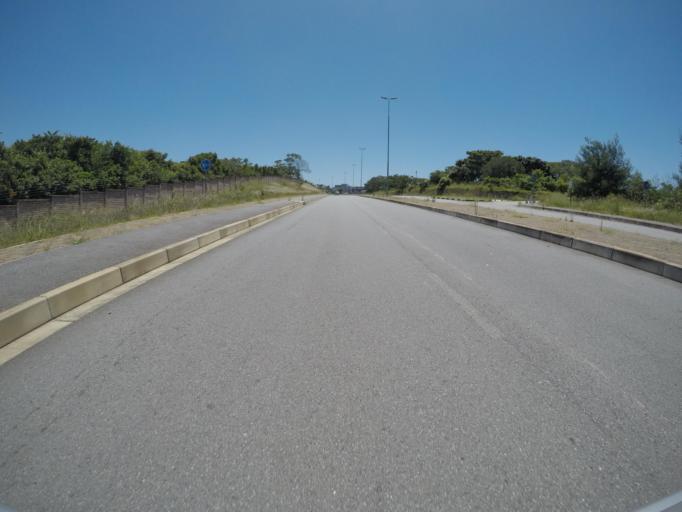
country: ZA
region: Eastern Cape
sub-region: Buffalo City Metropolitan Municipality
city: East London
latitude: -32.9515
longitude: 27.9477
